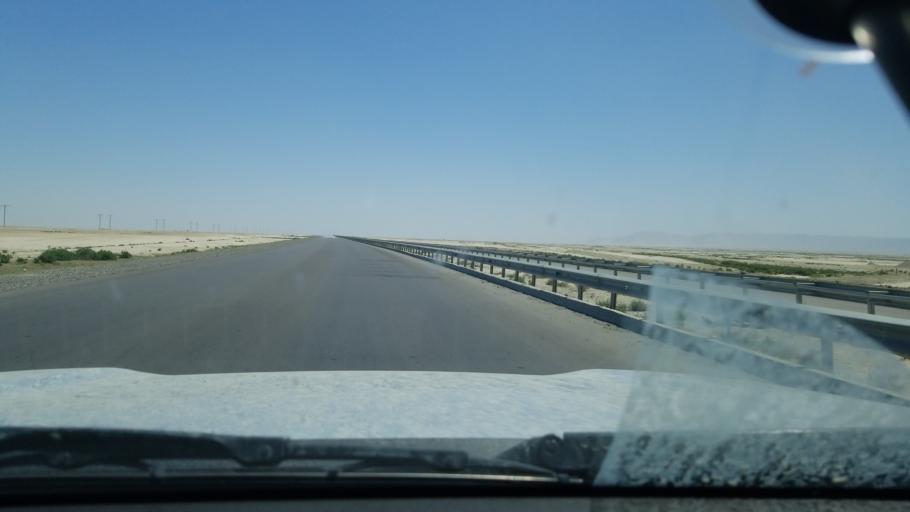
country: TM
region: Balkan
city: Gazanjyk
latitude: 39.2760
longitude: 55.1789
